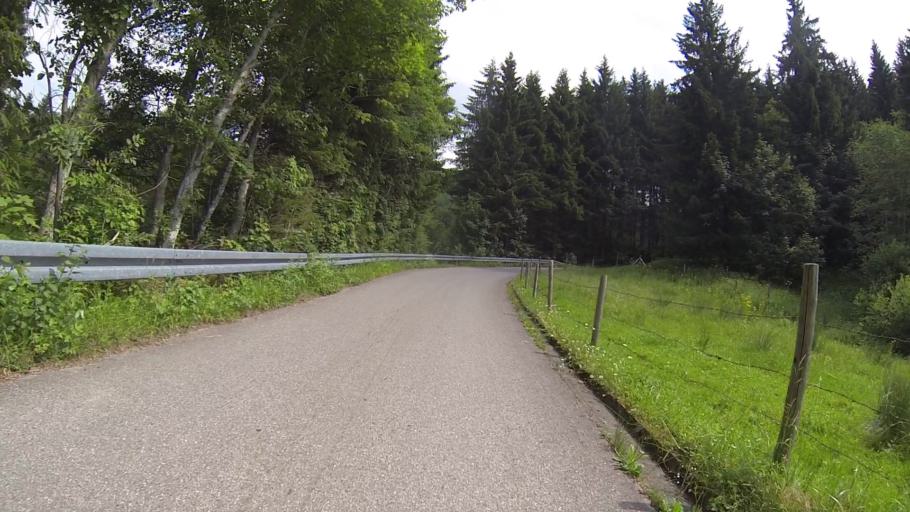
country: DE
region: Bavaria
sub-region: Swabia
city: Nesselwang
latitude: 47.6146
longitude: 10.4772
